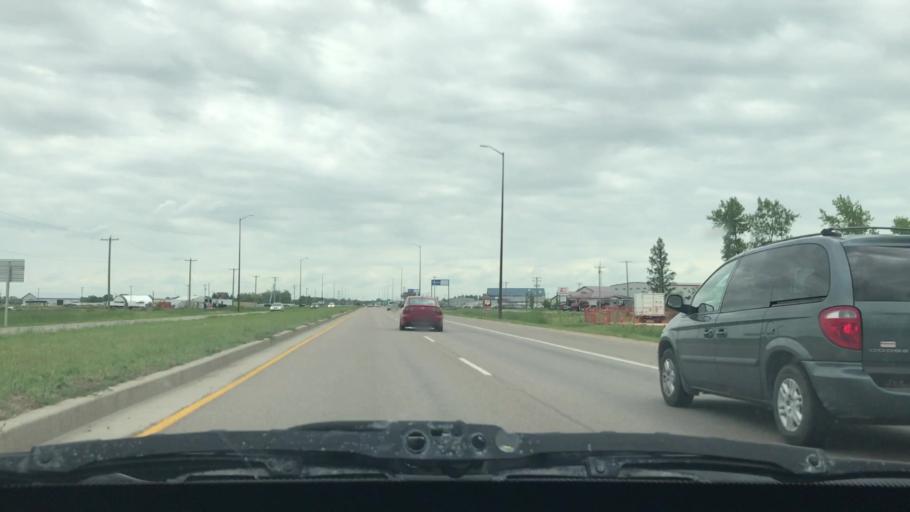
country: CA
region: Manitoba
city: Winnipeg
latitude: 49.8501
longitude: -97.0012
